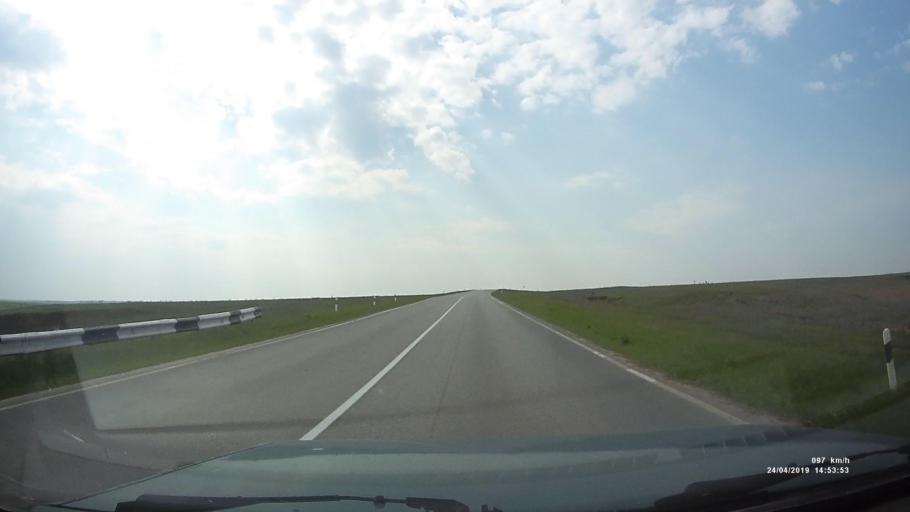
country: RU
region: Rostov
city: Remontnoye
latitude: 46.5319
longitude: 43.6495
